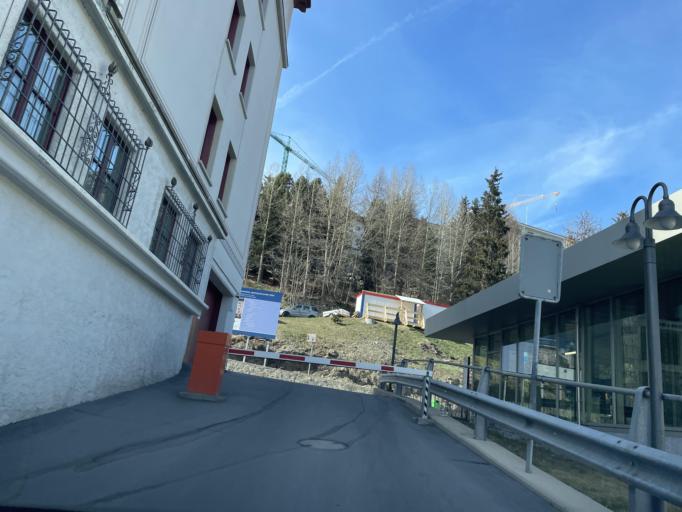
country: CH
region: Grisons
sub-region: Maloja District
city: Saint Moritz
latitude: 46.4975
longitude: 9.8413
